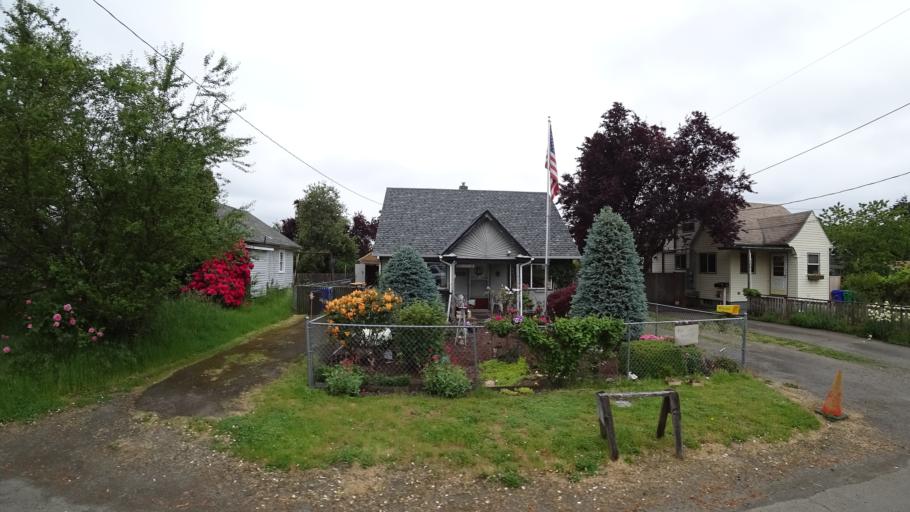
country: US
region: Oregon
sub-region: Multnomah County
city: Portland
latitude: 45.5525
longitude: -122.6091
